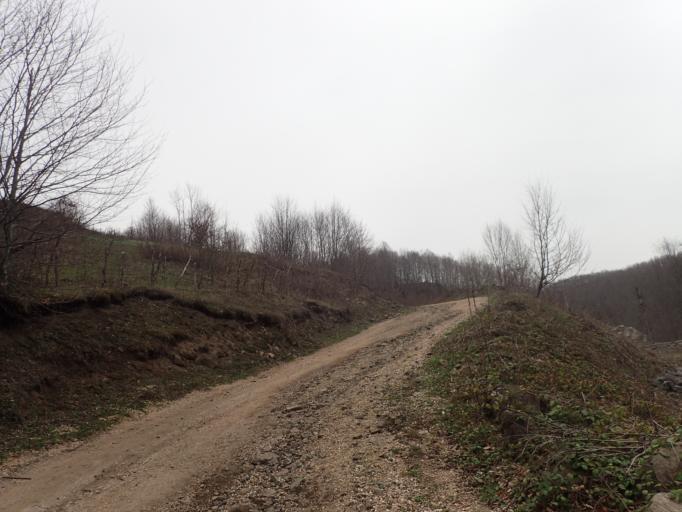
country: TR
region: Ordu
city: Kumru
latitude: 40.7949
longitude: 37.1767
